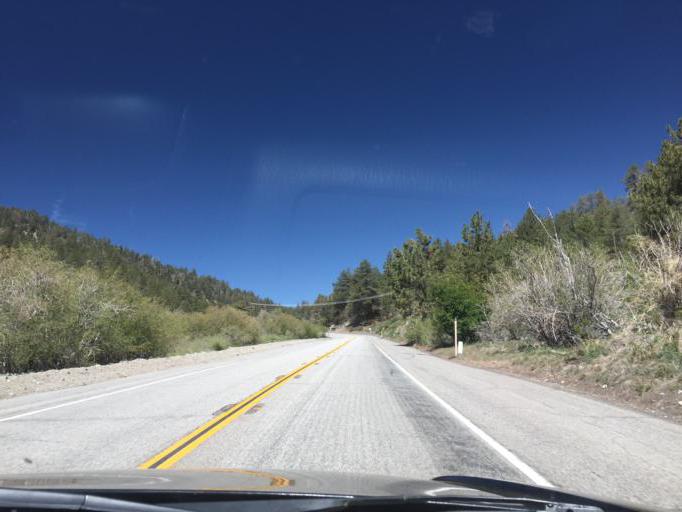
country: US
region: California
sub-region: San Bernardino County
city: Wrightwood
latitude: 34.3723
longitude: -117.6740
